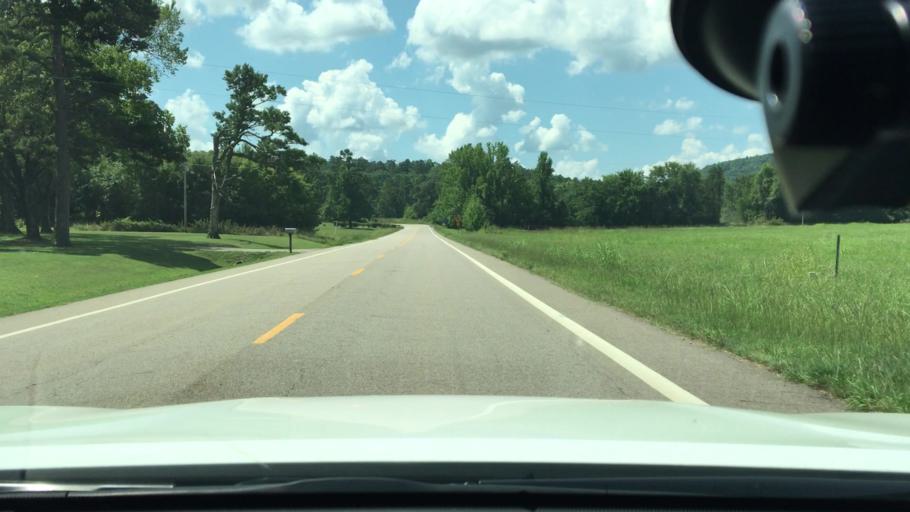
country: US
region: Arkansas
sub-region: Logan County
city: Paris
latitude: 35.2608
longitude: -93.6833
